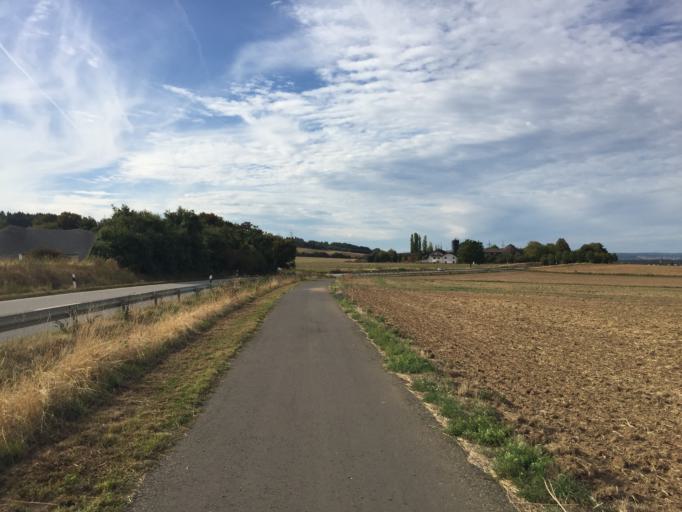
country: DE
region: Hesse
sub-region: Regierungsbezirk Giessen
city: Langgons
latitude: 50.5159
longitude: 8.7245
